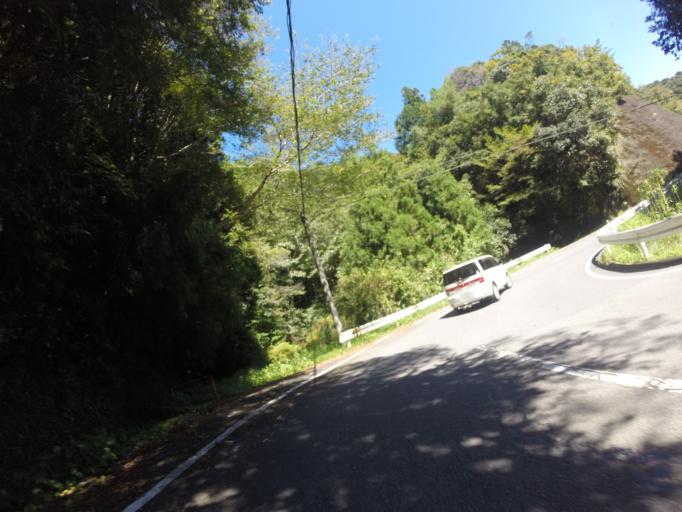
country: JP
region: Shizuoka
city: Kanaya
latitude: 34.9097
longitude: 138.1220
